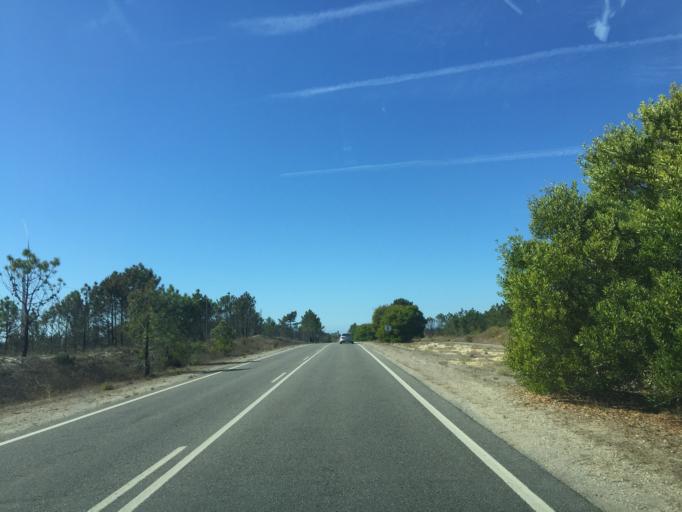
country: PT
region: Coimbra
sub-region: Mira
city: Mira
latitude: 40.3254
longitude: -8.8128
